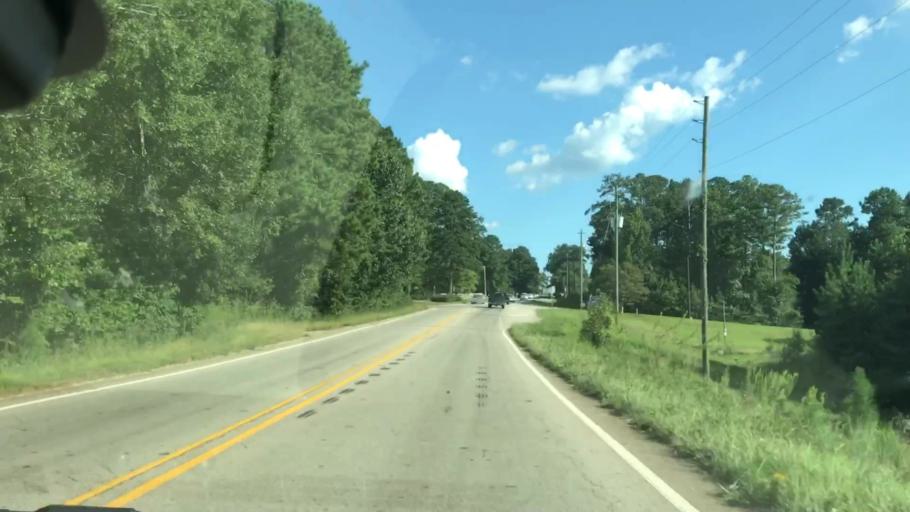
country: US
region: Georgia
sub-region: Troup County
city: La Grange
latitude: 32.9909
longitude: -85.0042
